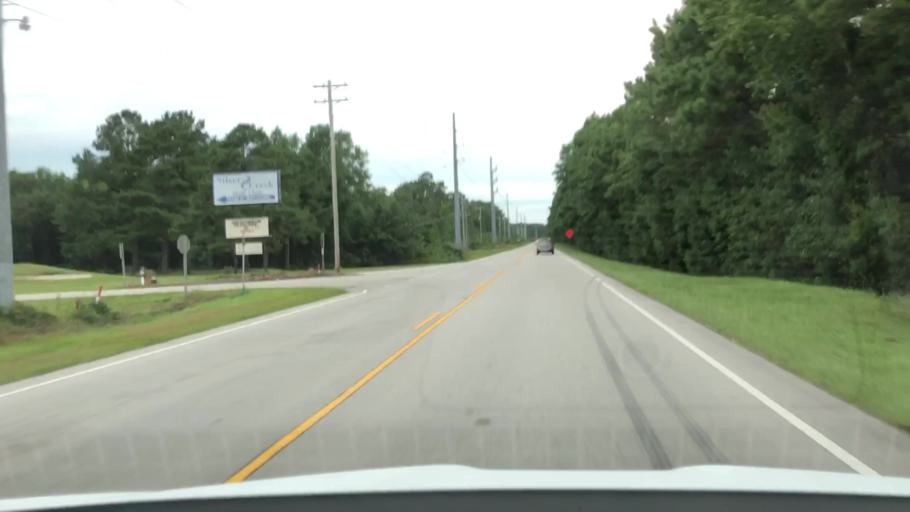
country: US
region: North Carolina
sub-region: Carteret County
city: Cape Carteret
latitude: 34.7402
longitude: -77.0857
